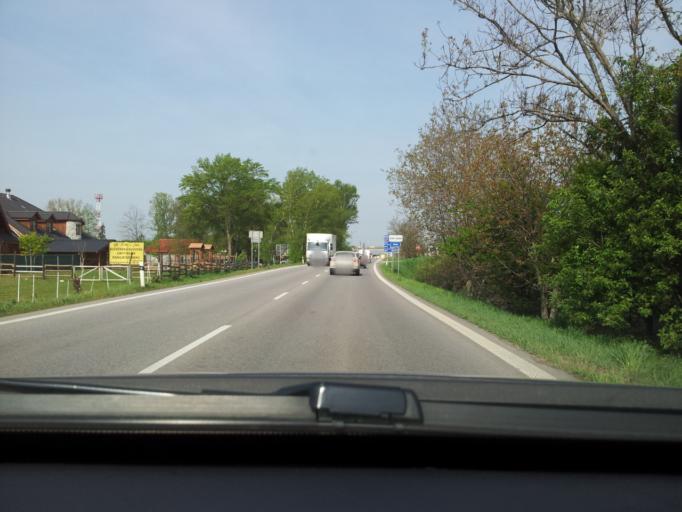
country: SK
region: Nitriansky
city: Levice
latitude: 48.2015
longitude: 18.5261
